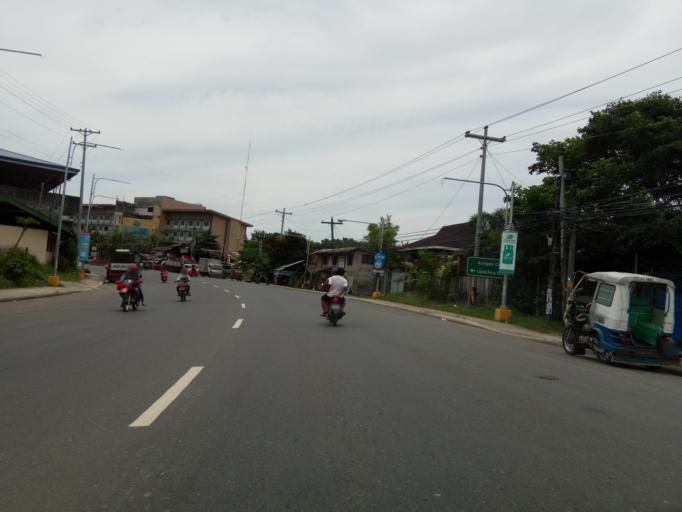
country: PH
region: Caraga
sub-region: Province of Surigao del Norte
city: Surigao
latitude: 9.7739
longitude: 125.4839
